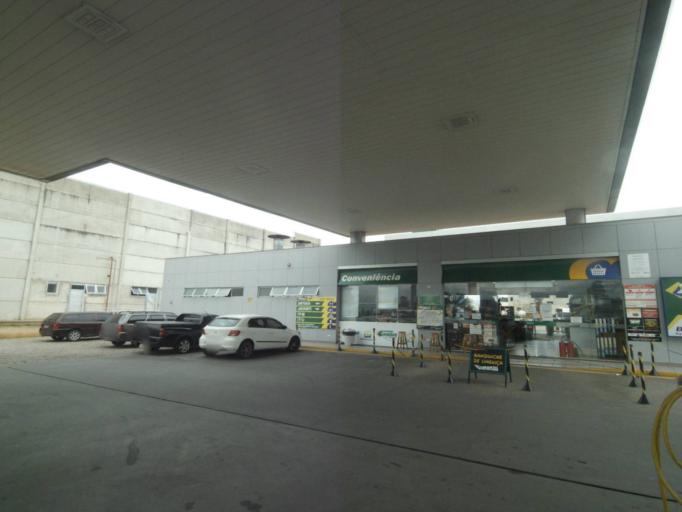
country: BR
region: Parana
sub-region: Sao Jose Dos Pinhais
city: Sao Jose dos Pinhais
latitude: -25.5480
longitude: -49.2850
